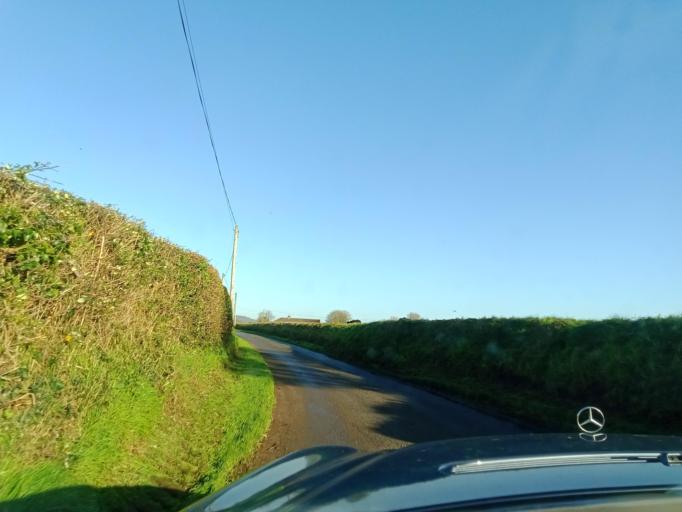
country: IE
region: Leinster
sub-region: Kilkenny
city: Mooncoin
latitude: 52.2883
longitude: -7.2111
